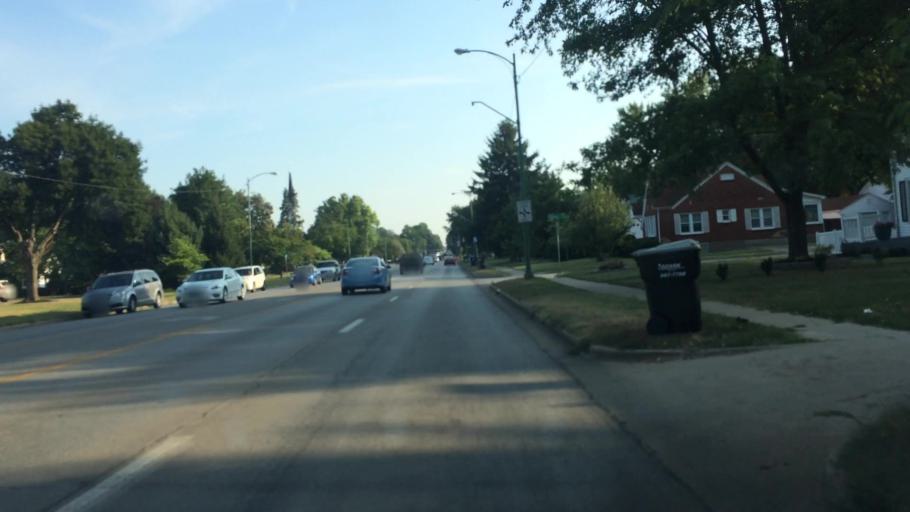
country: US
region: Missouri
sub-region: Greene County
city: Springfield
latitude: 37.1835
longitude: -93.2766
